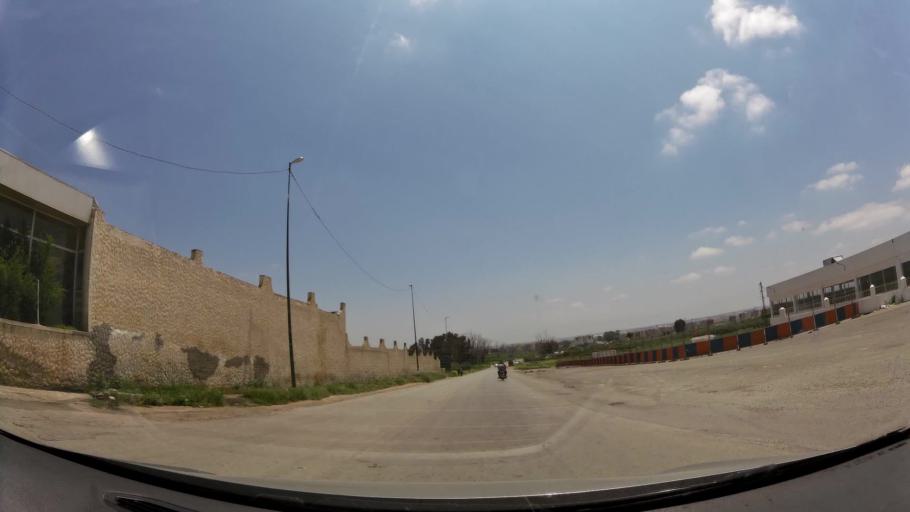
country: MA
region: Fes-Boulemane
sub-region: Fes
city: Fes
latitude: 34.0425
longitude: -5.0629
